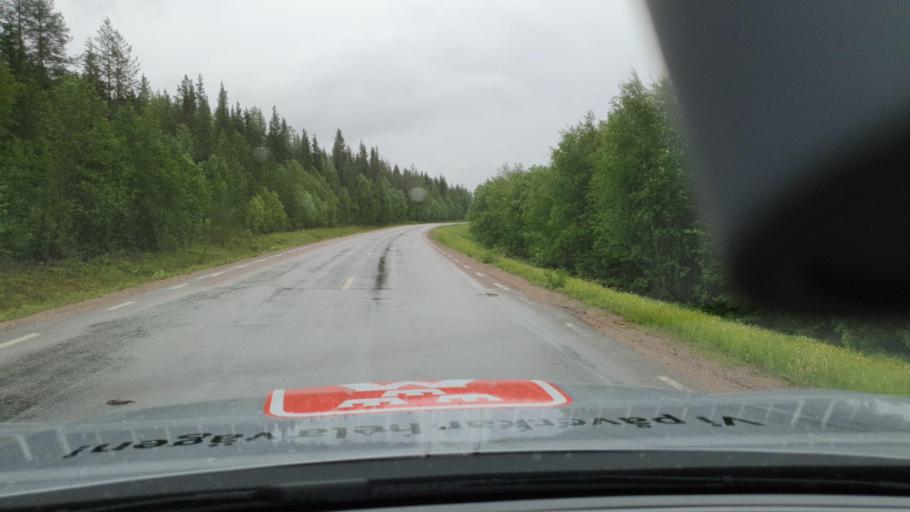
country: SE
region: Norrbotten
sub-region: Overtornea Kommun
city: OEvertornea
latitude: 66.4352
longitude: 23.3336
